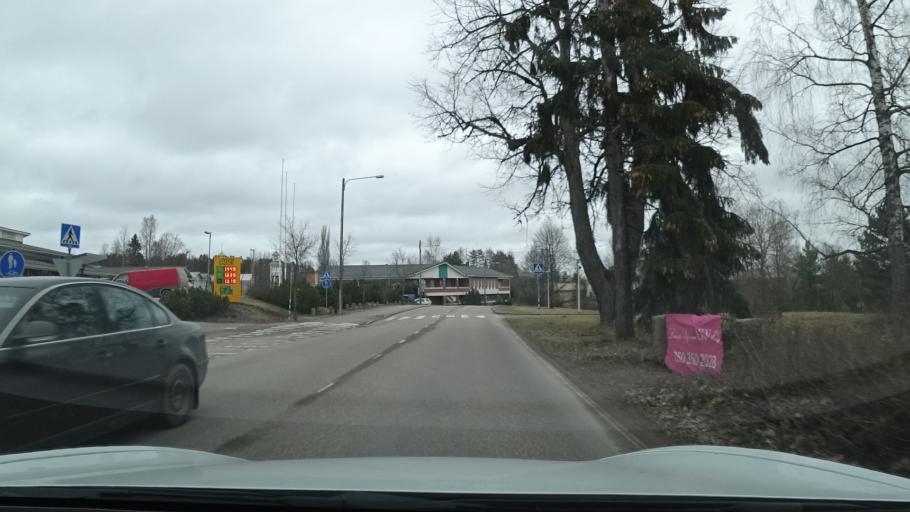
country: FI
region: Uusimaa
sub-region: Porvoo
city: Myrskylae
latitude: 60.6689
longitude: 25.8529
